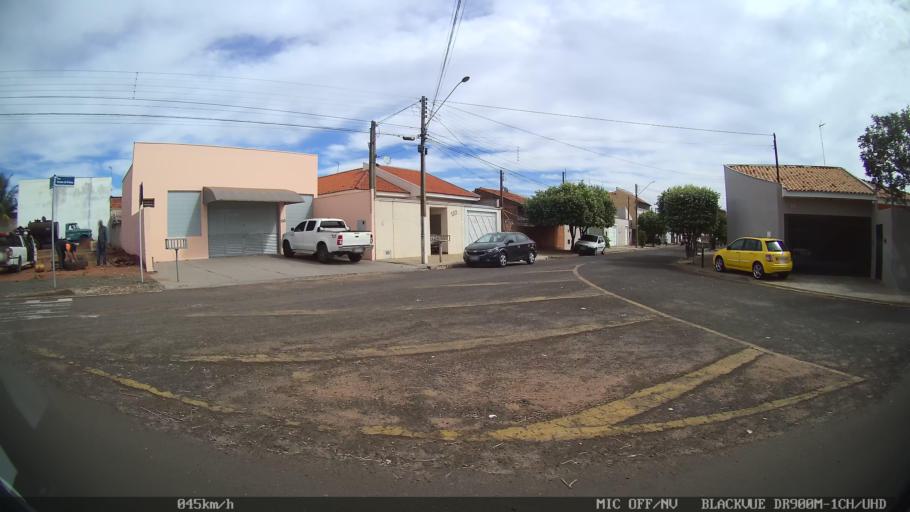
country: BR
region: Sao Paulo
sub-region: Catanduva
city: Catanduva
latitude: -21.1636
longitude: -48.9702
